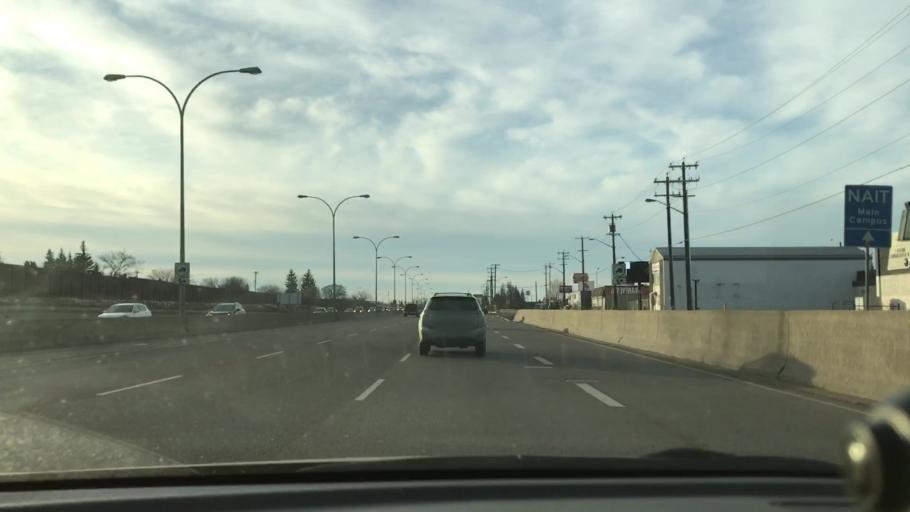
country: CA
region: Alberta
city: Edmonton
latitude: 53.5826
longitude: -113.4589
